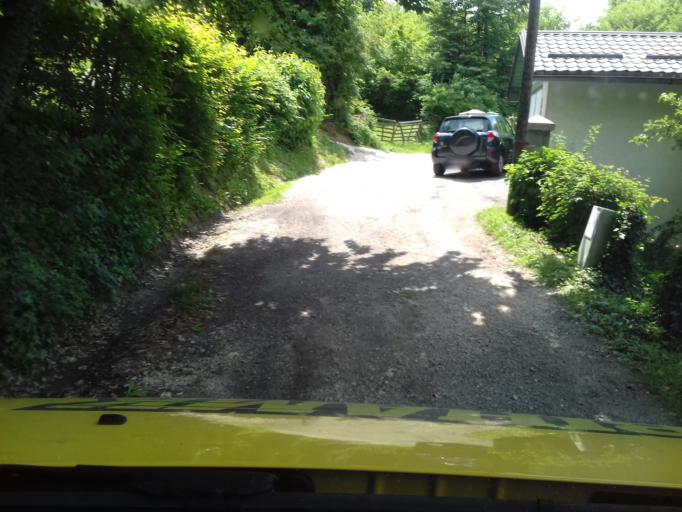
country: BA
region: Federation of Bosnia and Herzegovina
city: Hadzici
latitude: 43.8812
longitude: 18.1760
